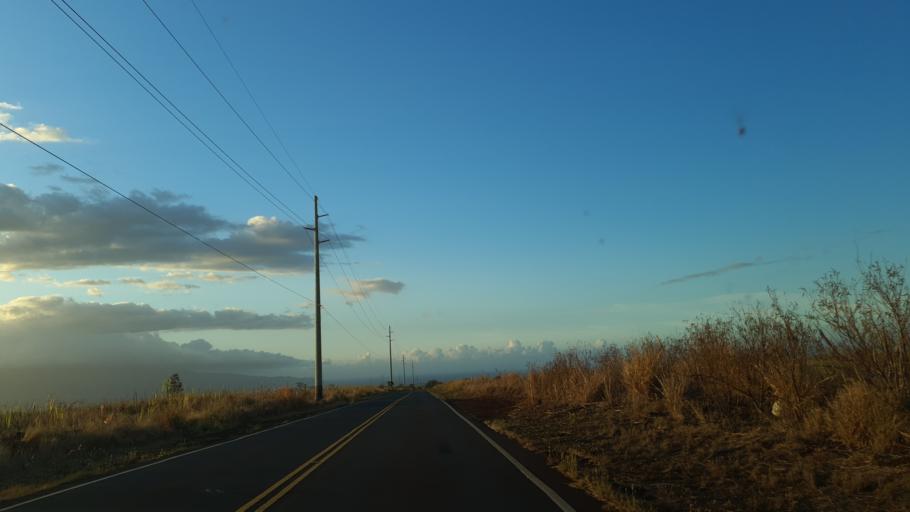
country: US
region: Hawaii
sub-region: Maui County
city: Pukalani
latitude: 20.8080
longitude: -156.3805
